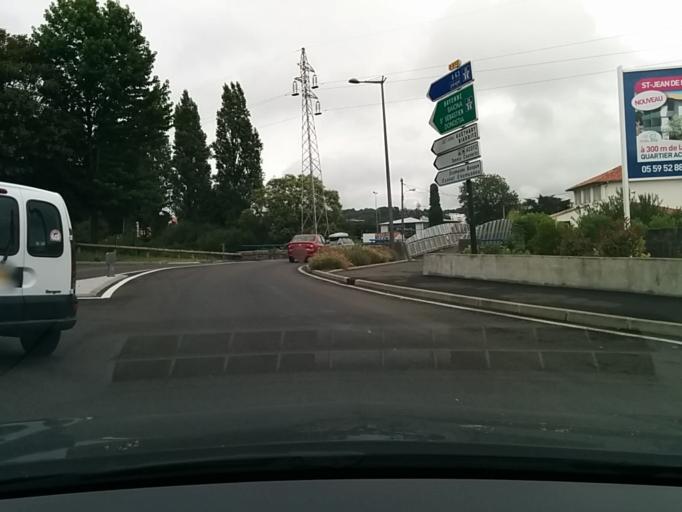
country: FR
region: Aquitaine
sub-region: Departement des Pyrenees-Atlantiques
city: Saint-Jean-de-Luz
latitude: 43.3971
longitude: -1.6445
